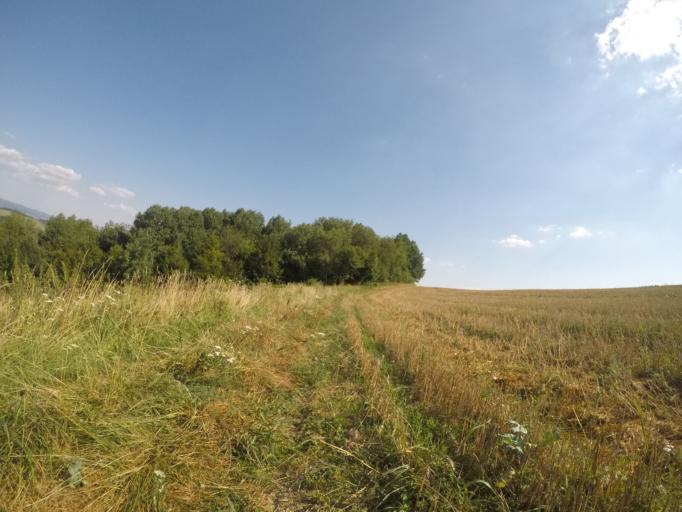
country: SK
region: Presovsky
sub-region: Okres Presov
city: Presov
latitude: 48.9365
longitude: 21.1689
